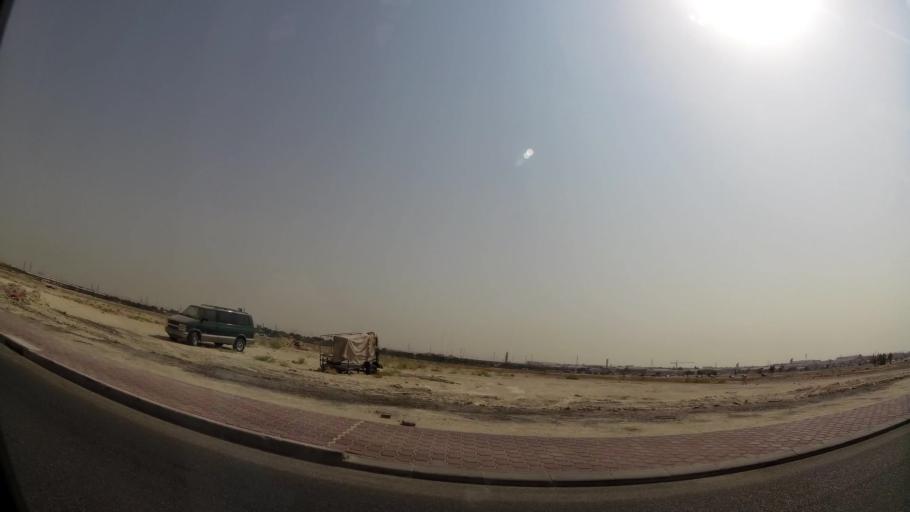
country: KW
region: Muhafazat al Jahra'
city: Al Jahra'
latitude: 29.3198
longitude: 47.7419
